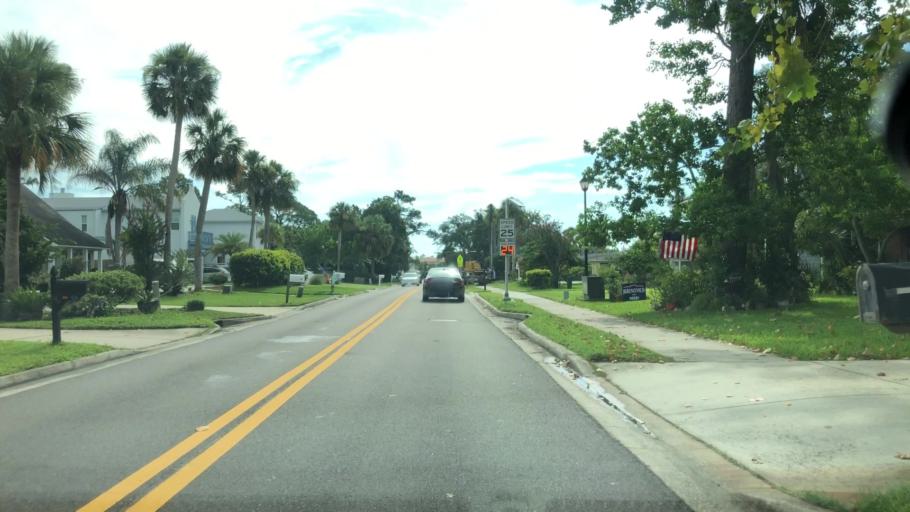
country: US
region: Florida
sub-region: Saint Johns County
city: Ponte Vedra Beach
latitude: 30.2274
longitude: -81.3831
